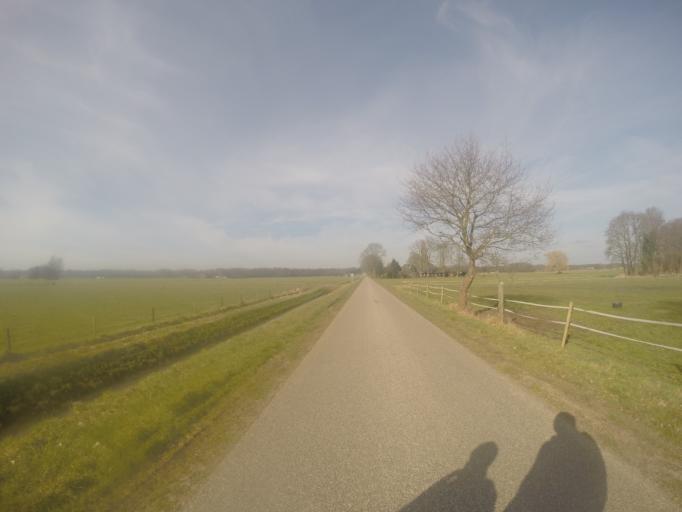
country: NL
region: Gelderland
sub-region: Gemeente Lochem
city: Lochem
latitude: 52.1232
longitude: 6.3815
